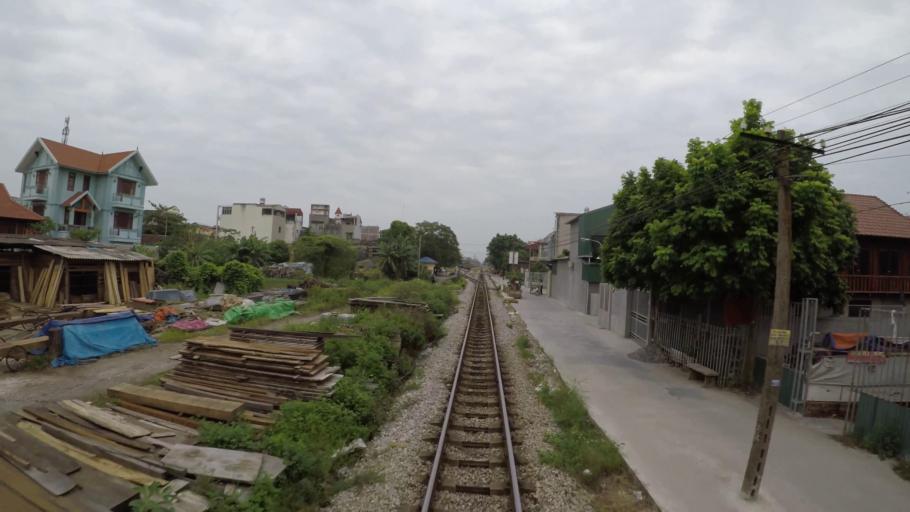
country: VN
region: Hai Duong
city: Thanh Pho Hai Duong
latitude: 20.9431
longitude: 106.2929
